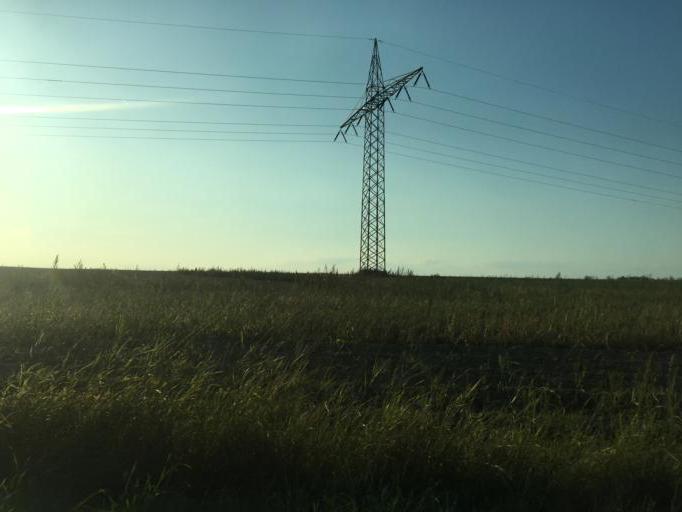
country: DE
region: Saxony
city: Coswig
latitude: 51.0724
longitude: 13.5964
